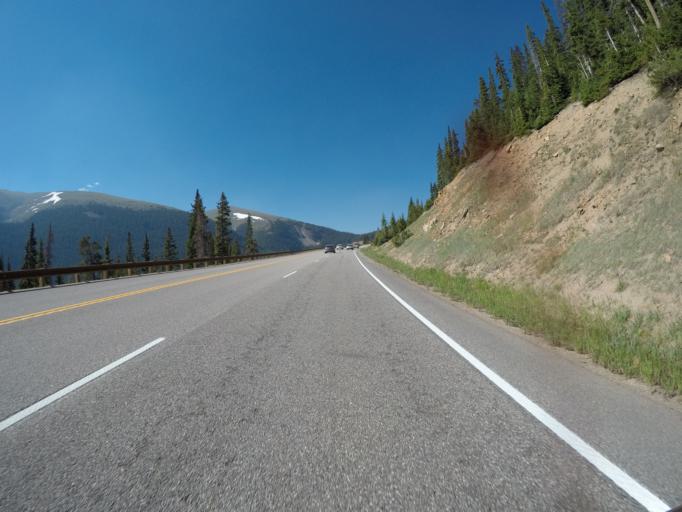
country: US
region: Colorado
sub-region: Clear Creek County
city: Georgetown
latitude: 39.8190
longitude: -105.7688
